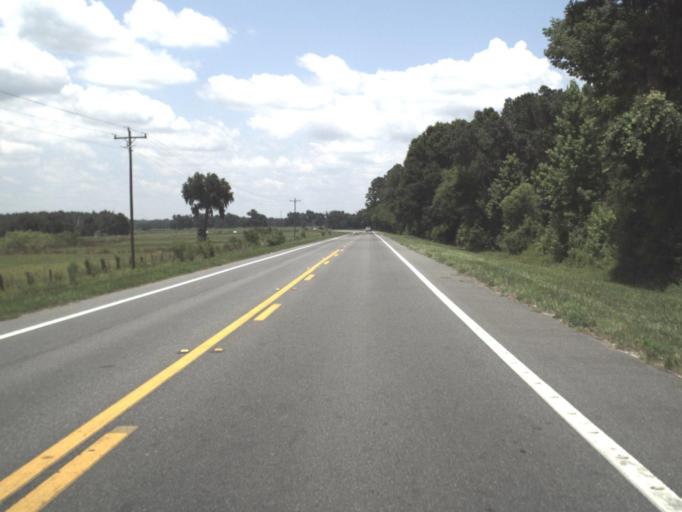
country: US
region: Florida
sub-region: Levy County
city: Williston
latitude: 29.4506
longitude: -82.4109
